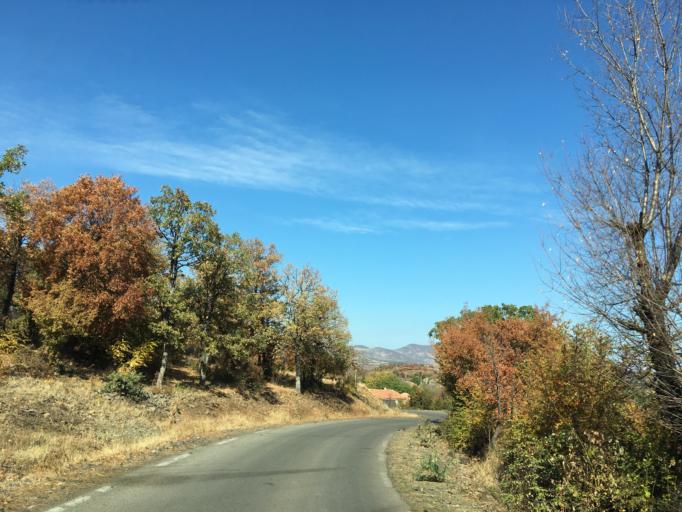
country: BG
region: Kurdzhali
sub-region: Obshtina Krumovgrad
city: Krumovgrad
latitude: 41.4949
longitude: 25.5274
